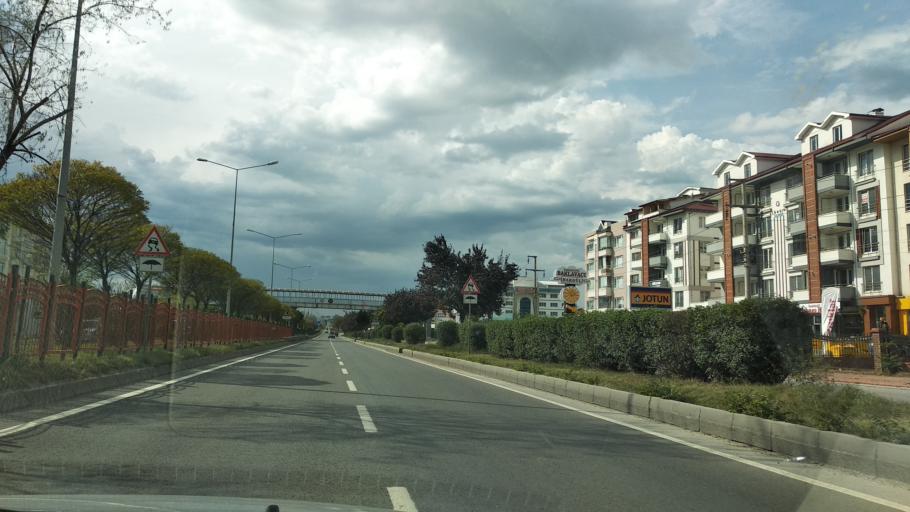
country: TR
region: Bolu
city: Bolu
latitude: 40.7367
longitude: 31.5936
